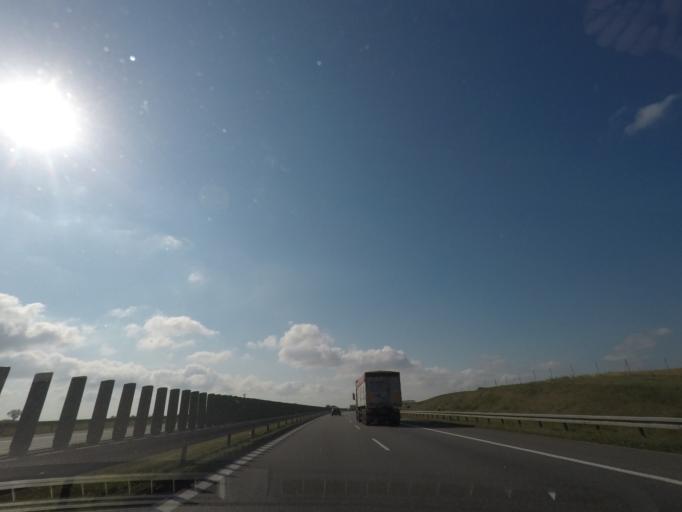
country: PL
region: Pomeranian Voivodeship
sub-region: Powiat gdanski
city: Pszczolki
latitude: 54.1758
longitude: 18.6503
